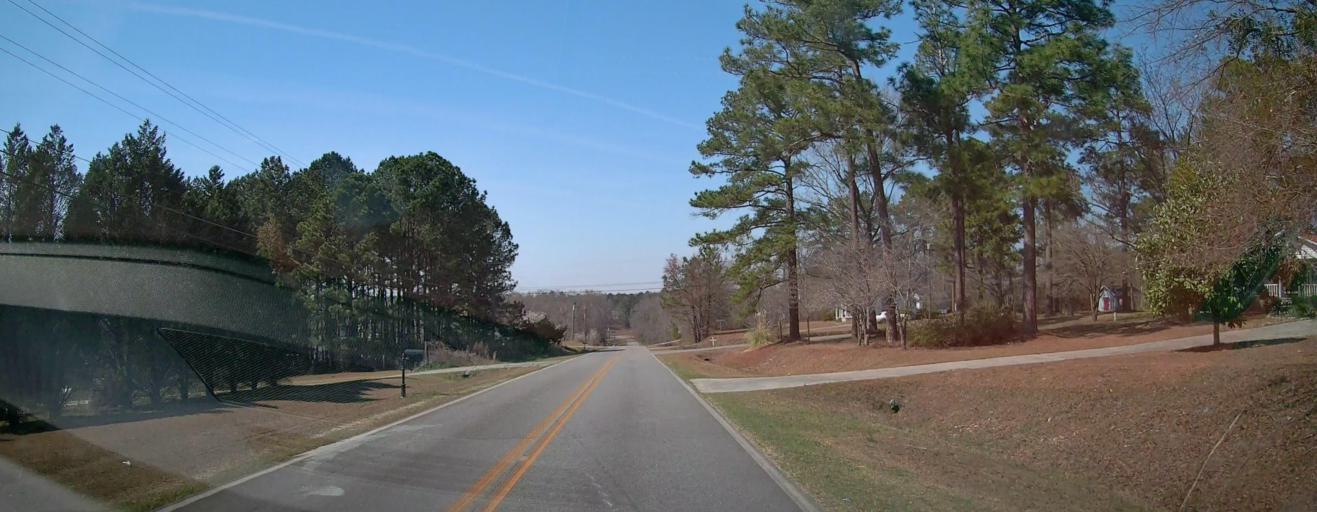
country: US
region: Georgia
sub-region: Jones County
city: Gray
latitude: 32.9019
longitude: -83.5414
